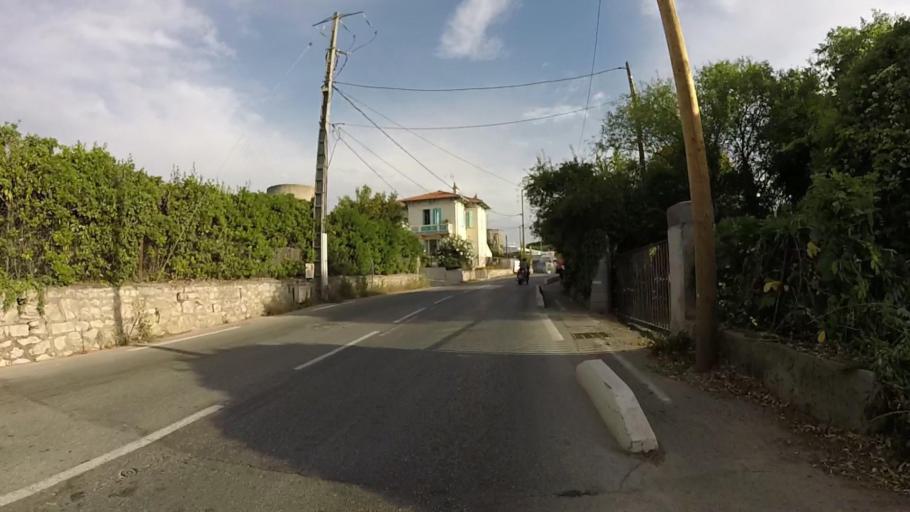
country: FR
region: Provence-Alpes-Cote d'Azur
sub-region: Departement des Alpes-Maritimes
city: Biot
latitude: 43.6041
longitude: 7.1125
